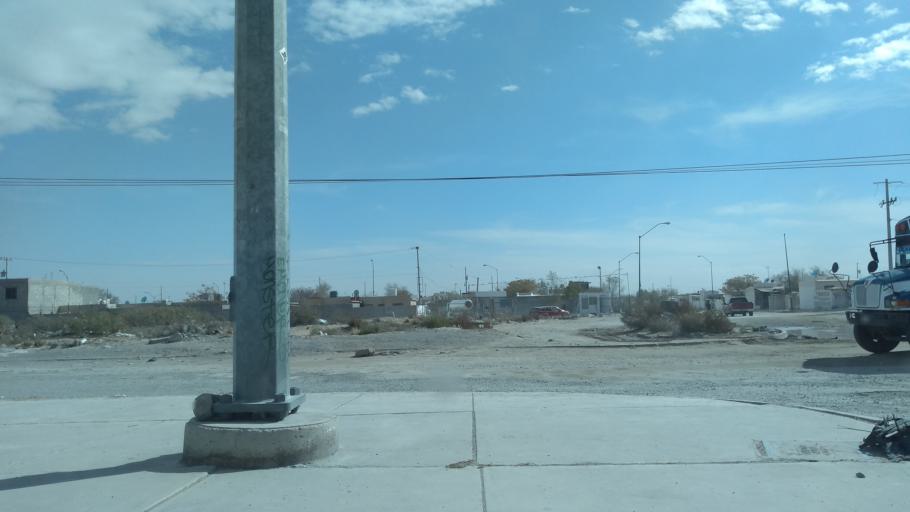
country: US
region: Texas
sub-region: El Paso County
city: San Elizario
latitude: 31.5691
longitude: -106.3426
